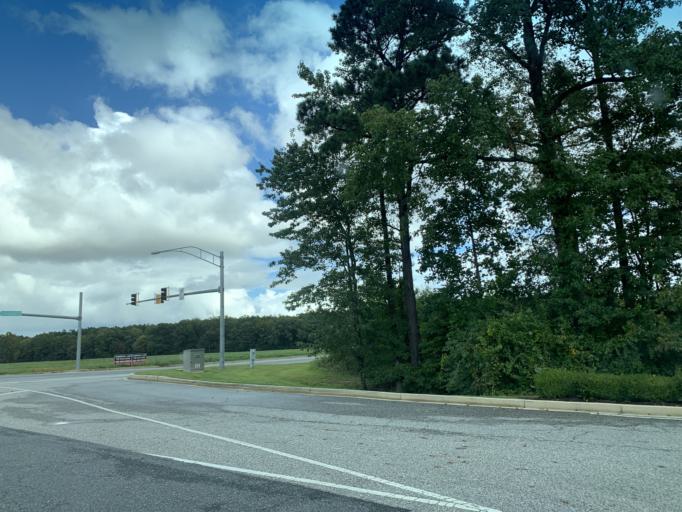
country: US
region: Maryland
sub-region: Caroline County
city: Denton
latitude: 38.8752
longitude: -75.8201
